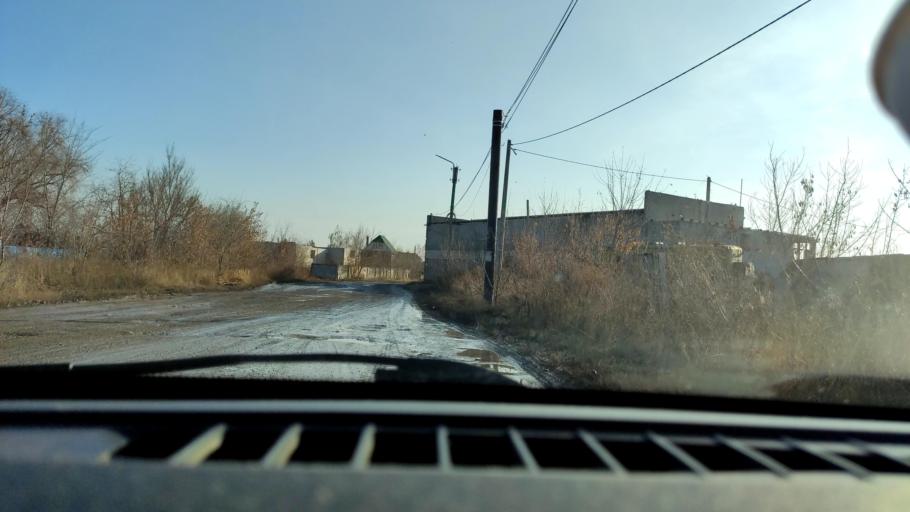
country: RU
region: Samara
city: Samara
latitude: 53.1183
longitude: 50.1113
